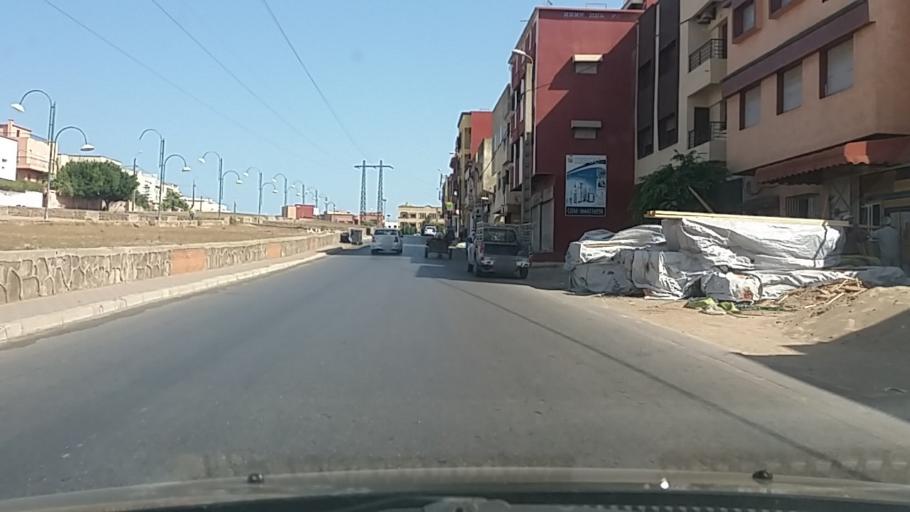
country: MA
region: Gharb-Chrarda-Beni Hssen
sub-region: Kenitra Province
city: Kenitra
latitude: 34.2638
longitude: -6.6167
